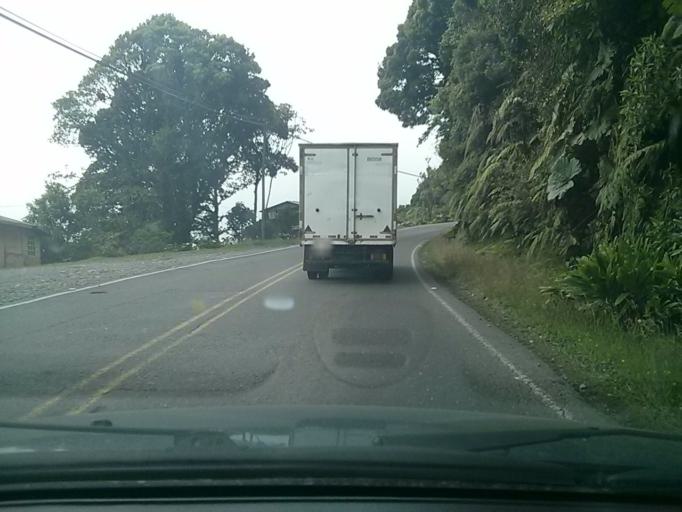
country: CR
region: Cartago
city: Tobosi
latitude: 9.7399
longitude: -83.9514
